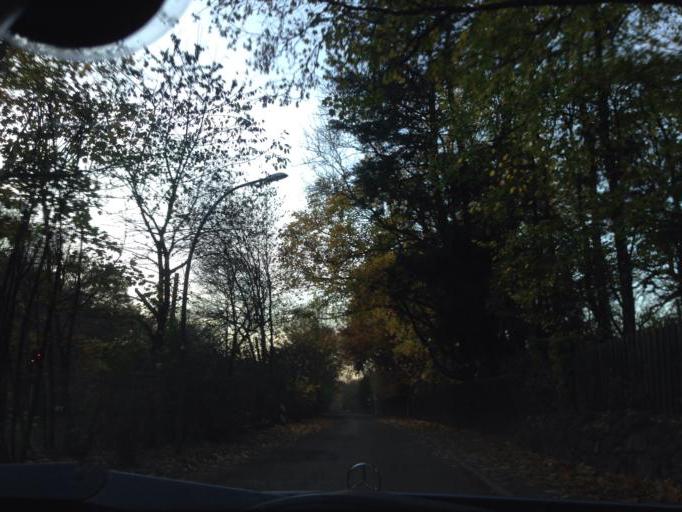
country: DE
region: Schleswig-Holstein
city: Aumuhle
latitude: 53.5292
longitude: 10.3341
